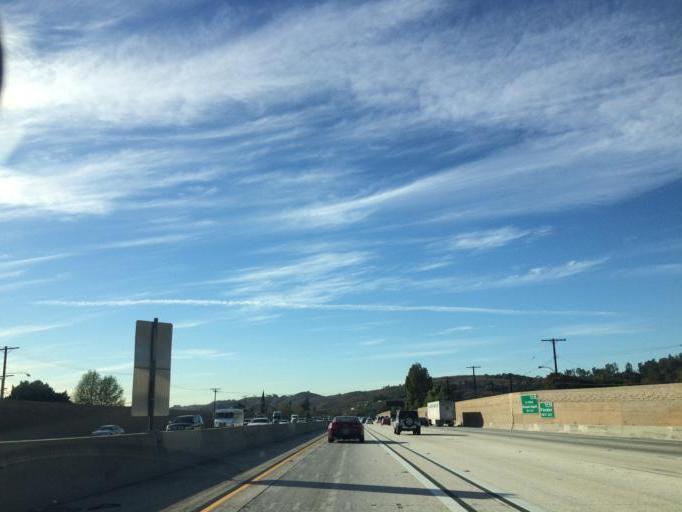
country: US
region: California
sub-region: Los Angeles County
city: Pomona
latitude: 34.0712
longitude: -117.7652
